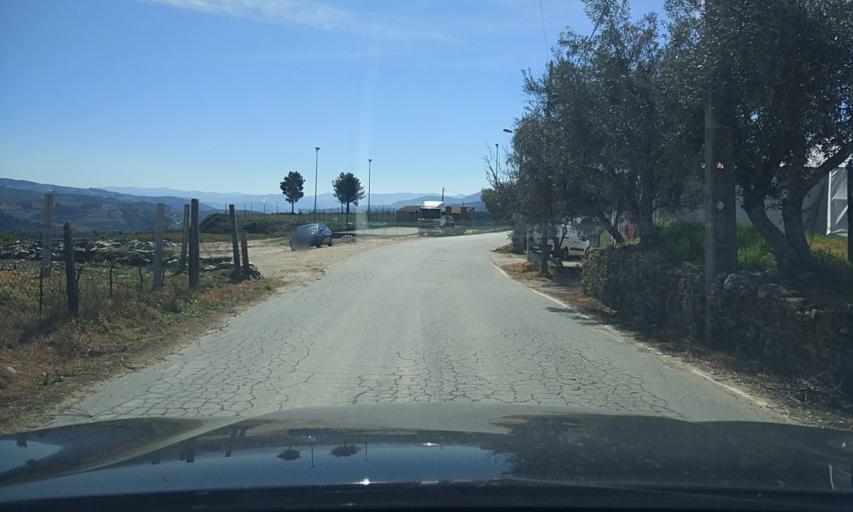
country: PT
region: Vila Real
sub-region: Sabrosa
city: Sabrosa
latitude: 41.3224
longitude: -7.5552
